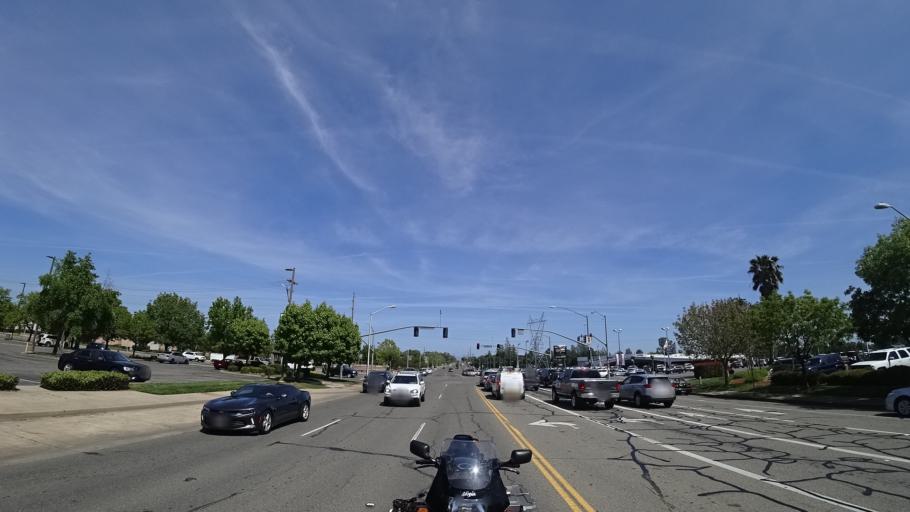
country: US
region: California
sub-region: Shasta County
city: Redding
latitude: 40.5712
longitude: -122.3538
